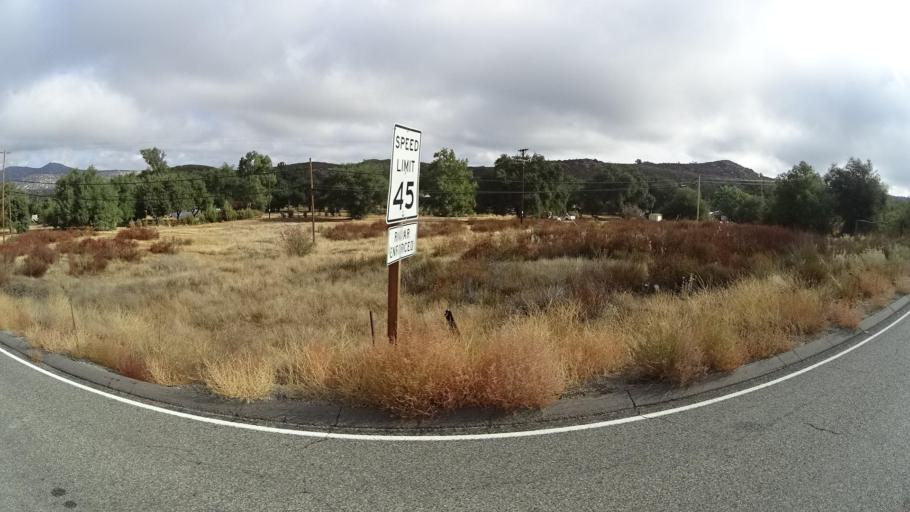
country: MX
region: Baja California
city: Tecate
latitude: 32.6034
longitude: -116.6065
